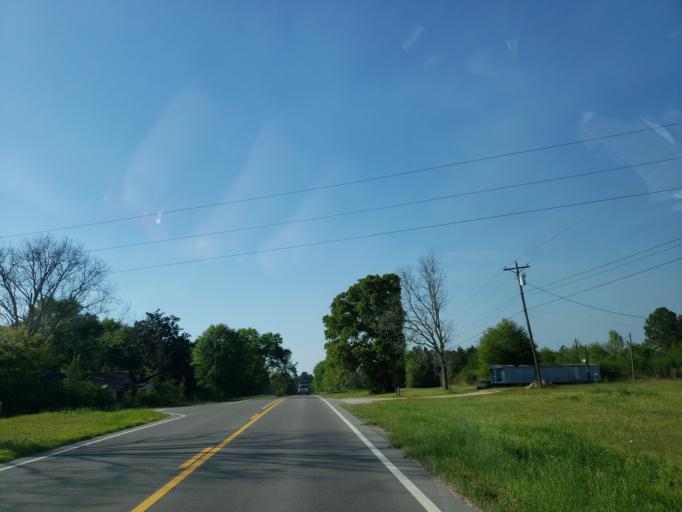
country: US
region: Mississippi
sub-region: Perry County
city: Richton
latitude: 31.4265
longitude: -88.9621
